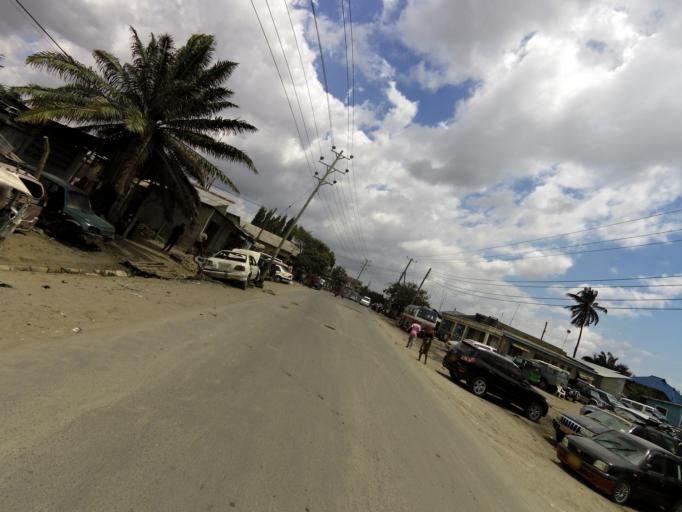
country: TZ
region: Dar es Salaam
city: Magomeni
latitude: -6.7904
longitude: 39.2324
